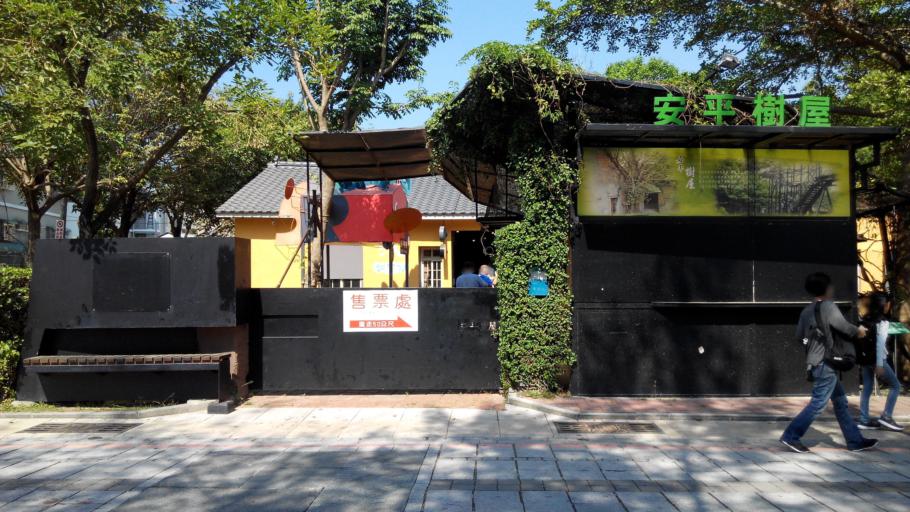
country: TW
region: Taiwan
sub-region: Tainan
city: Tainan
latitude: 23.0032
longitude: 120.1595
